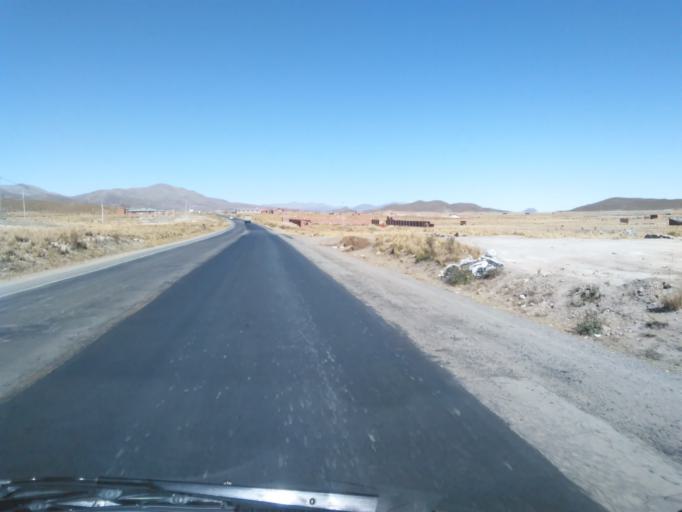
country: BO
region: Oruro
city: Oruro
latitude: -18.0068
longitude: -67.0396
